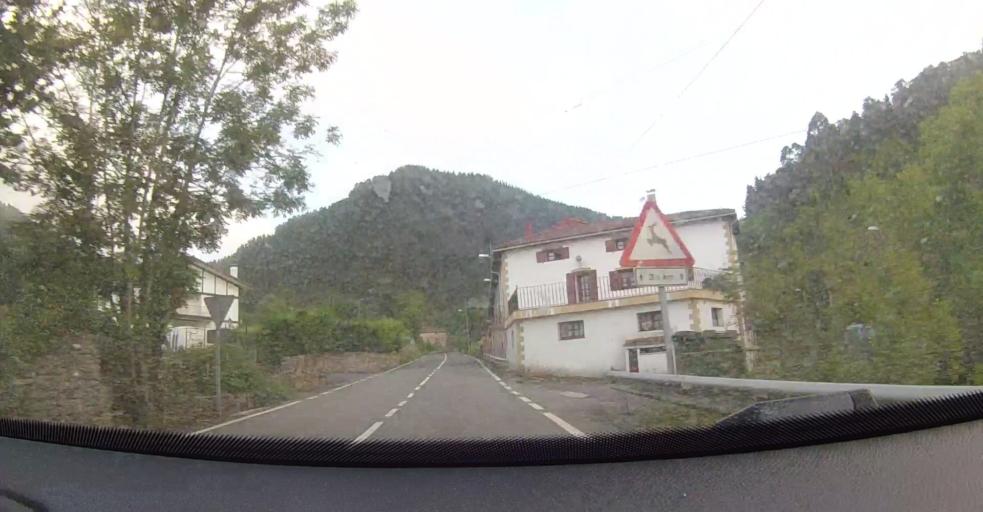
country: ES
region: Basque Country
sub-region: Bizkaia
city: Sopuerta
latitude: 43.2479
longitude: -3.1547
